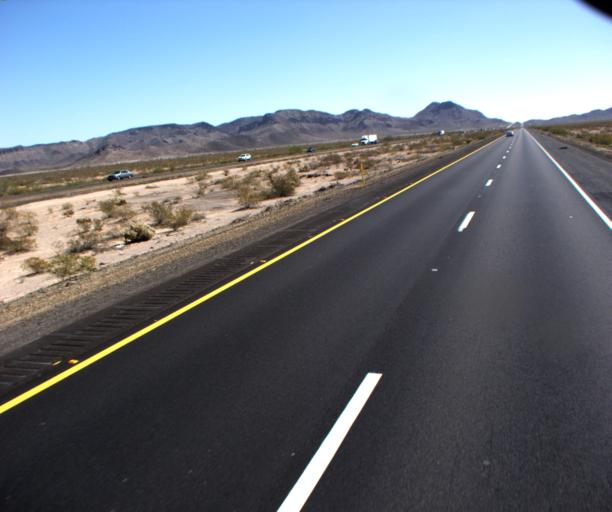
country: US
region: Arizona
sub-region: La Paz County
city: Salome
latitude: 33.6186
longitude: -113.6856
